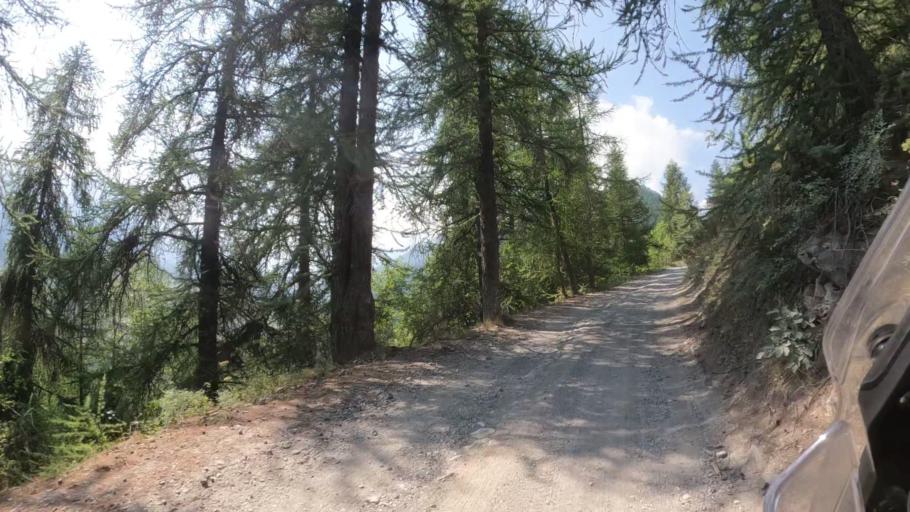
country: IT
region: Piedmont
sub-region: Provincia di Torino
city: Cesana Torinese
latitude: 44.9275
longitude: 6.8136
